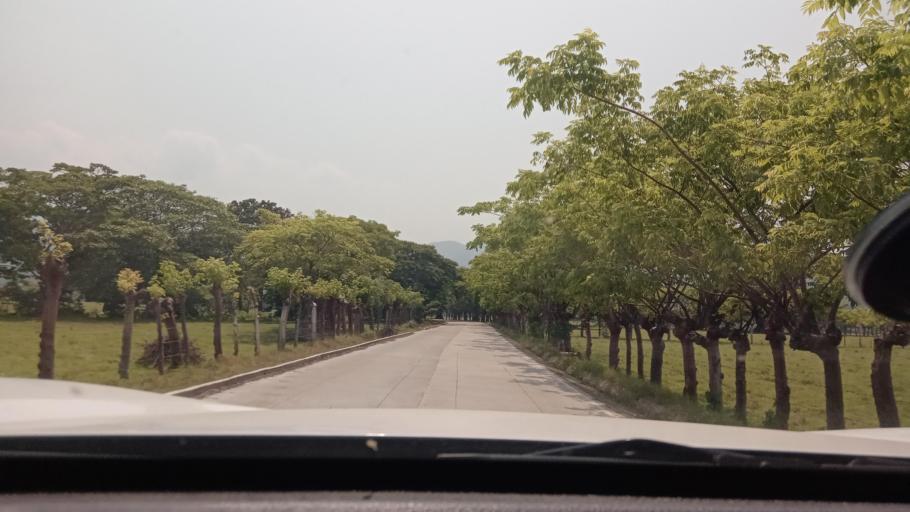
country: MX
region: Veracruz
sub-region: San Andres Tuxtla
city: Santa Rosa Abata
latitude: 18.5625
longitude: -95.0524
